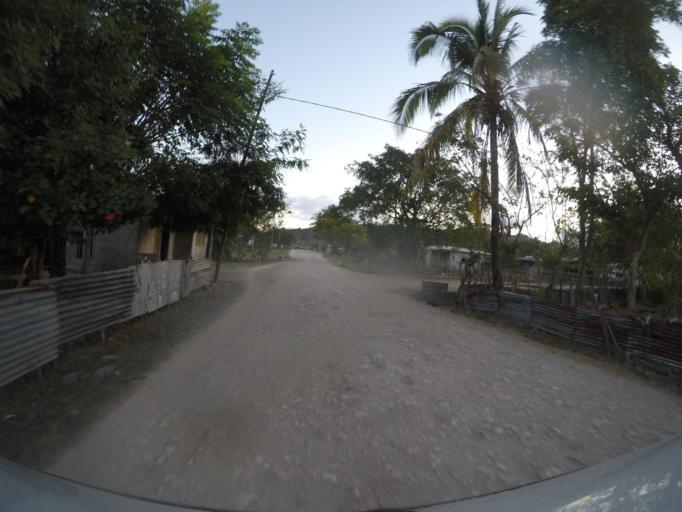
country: TL
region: Viqueque
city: Viqueque
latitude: -8.7756
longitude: 126.6375
